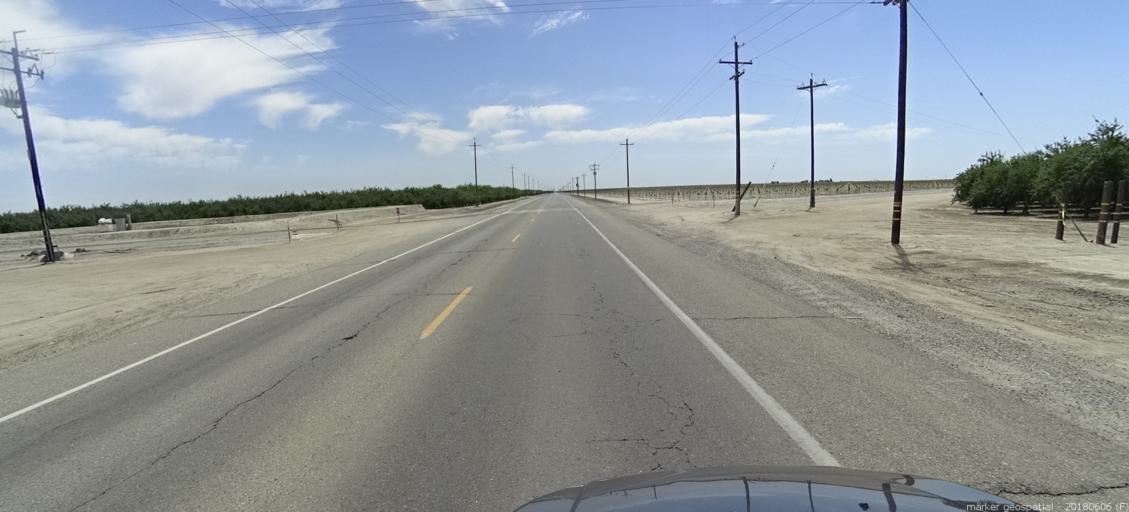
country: US
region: California
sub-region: Fresno County
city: Firebaugh
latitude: 36.8586
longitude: -120.3861
